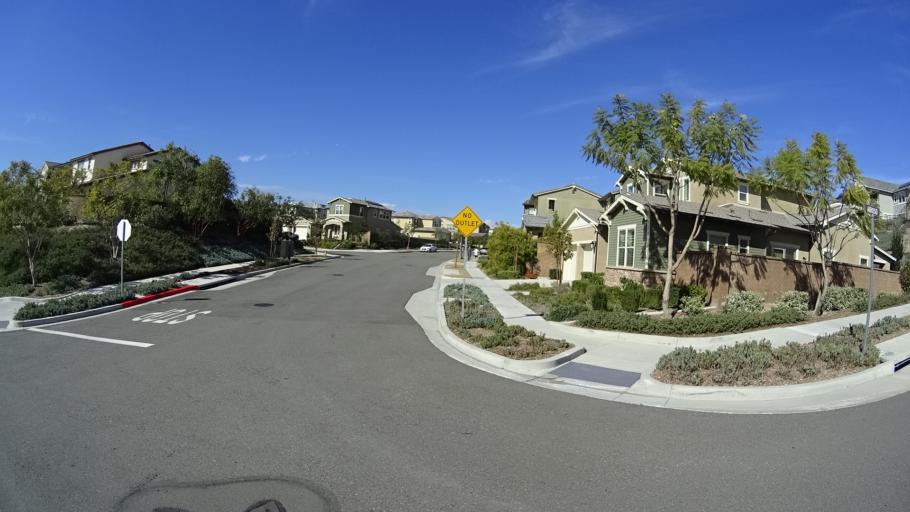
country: US
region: California
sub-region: Orange County
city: Ladera Ranch
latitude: 33.5389
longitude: -117.6047
